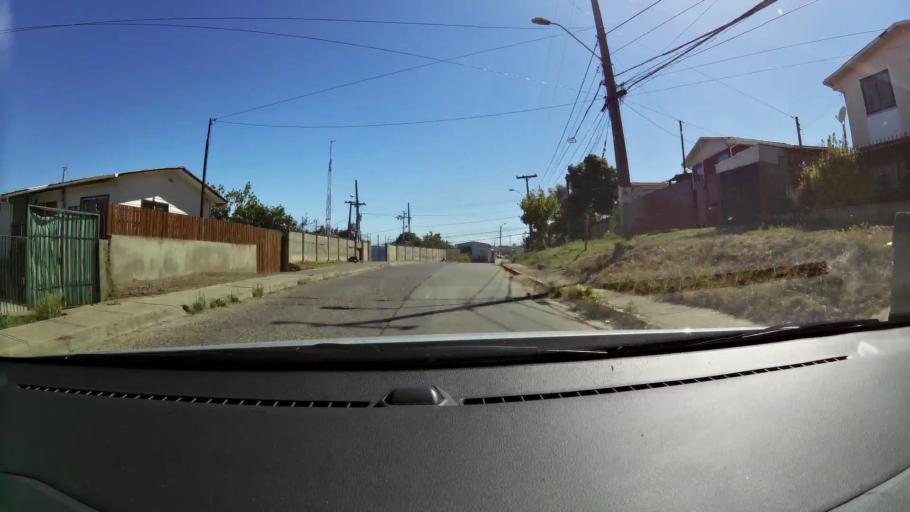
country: CL
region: Valparaiso
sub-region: Provincia de Valparaiso
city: Vina del Mar
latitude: -33.0599
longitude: -71.5762
